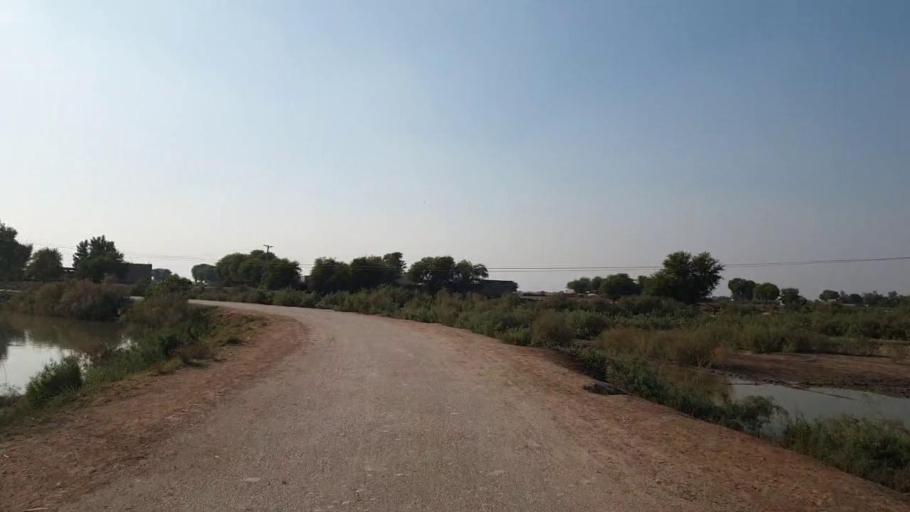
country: PK
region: Sindh
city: Sehwan
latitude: 26.4449
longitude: 67.8110
